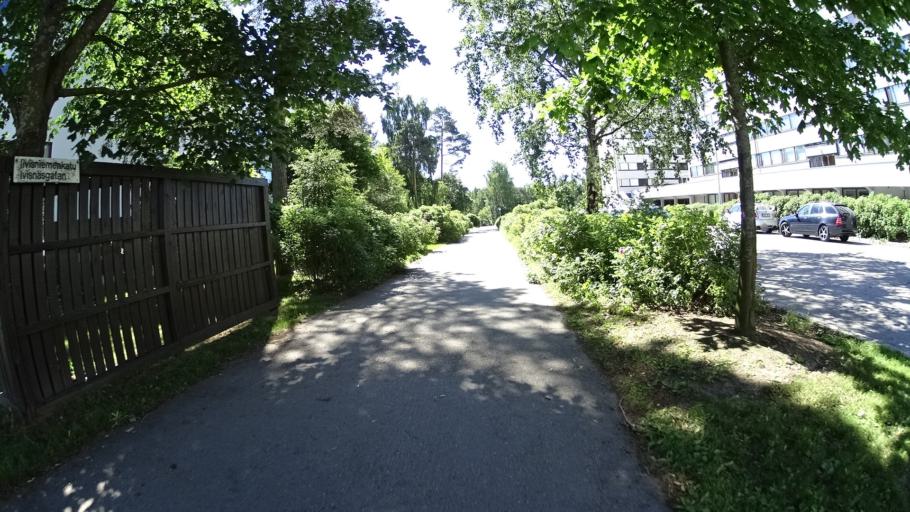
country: FI
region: Uusimaa
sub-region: Helsinki
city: Espoo
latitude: 60.1486
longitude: 24.6916
